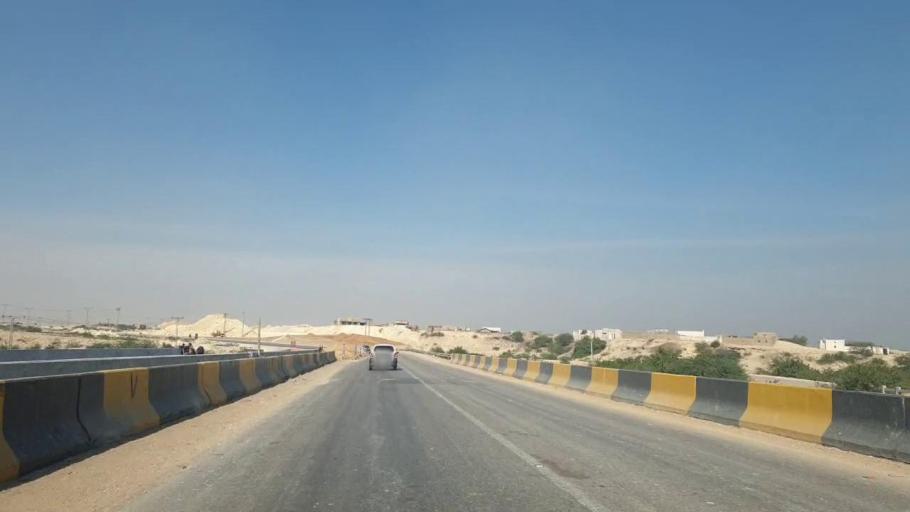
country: PK
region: Sindh
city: Hala
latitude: 25.7325
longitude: 68.2927
